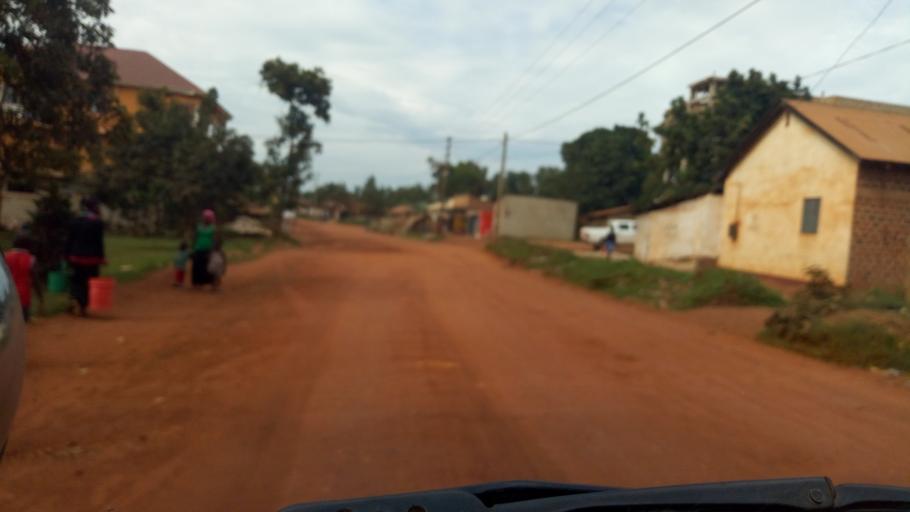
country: UG
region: Central Region
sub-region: Wakiso District
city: Bweyogerere
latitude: 0.3584
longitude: 32.7016
